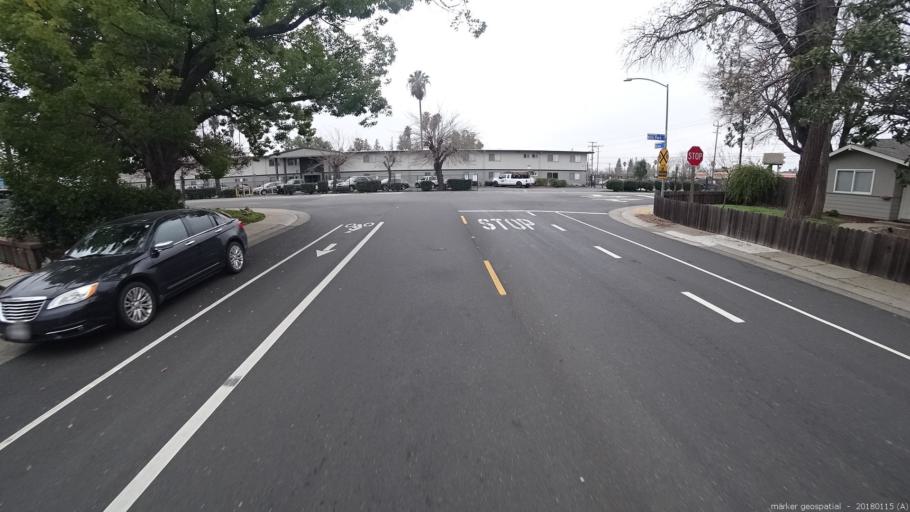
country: US
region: California
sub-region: Sacramento County
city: Rancho Cordova
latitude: 38.5917
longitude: -121.2959
